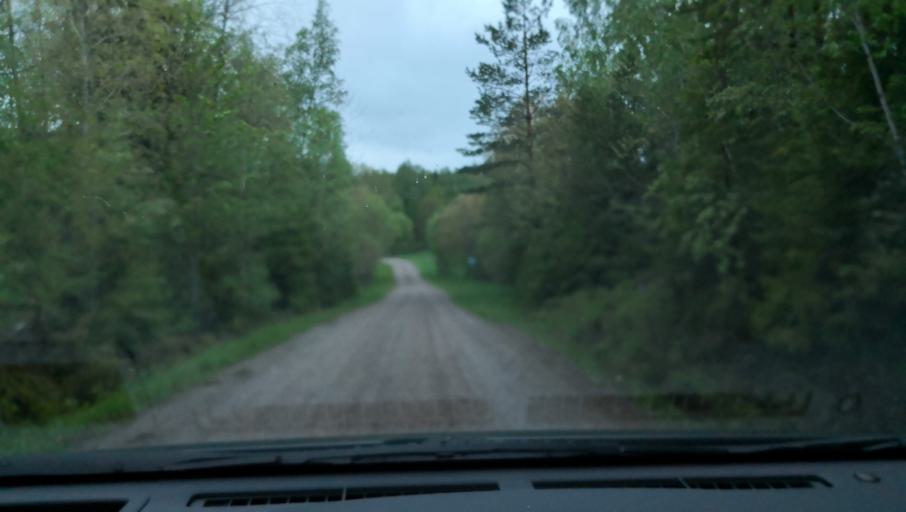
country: SE
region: Uppsala
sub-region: Heby Kommun
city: OEstervala
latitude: 59.9912
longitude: 17.2529
